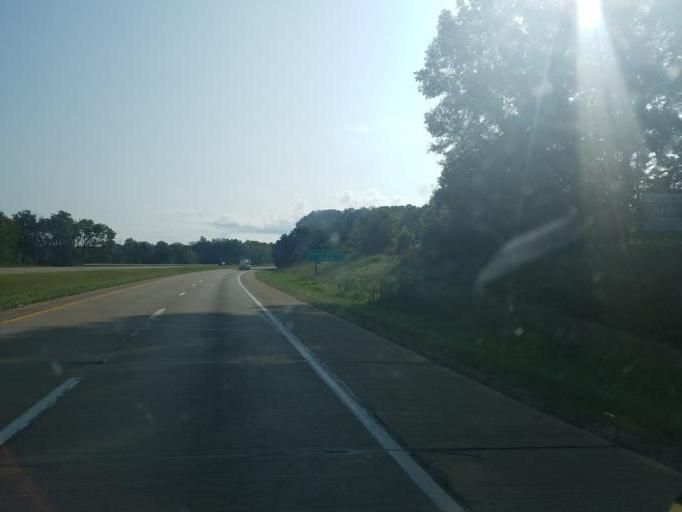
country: US
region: Ohio
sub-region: Ashland County
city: Ashland
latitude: 40.7861
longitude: -82.3500
